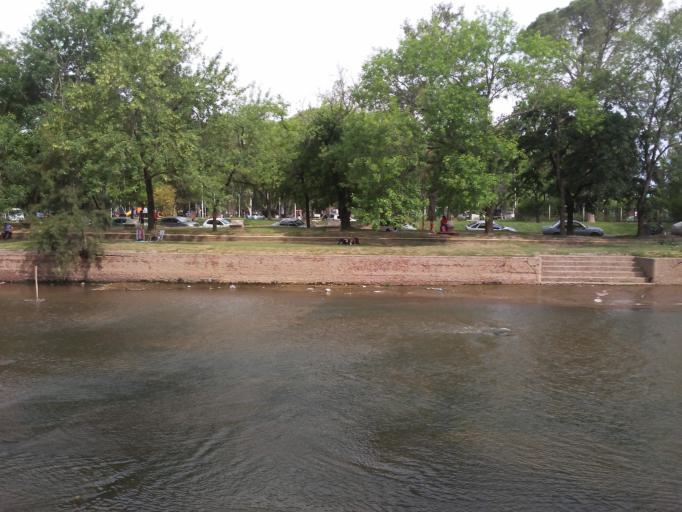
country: AR
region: Buenos Aires
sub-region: Partido de Mercedes
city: Mercedes
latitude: -34.6335
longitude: -59.4351
